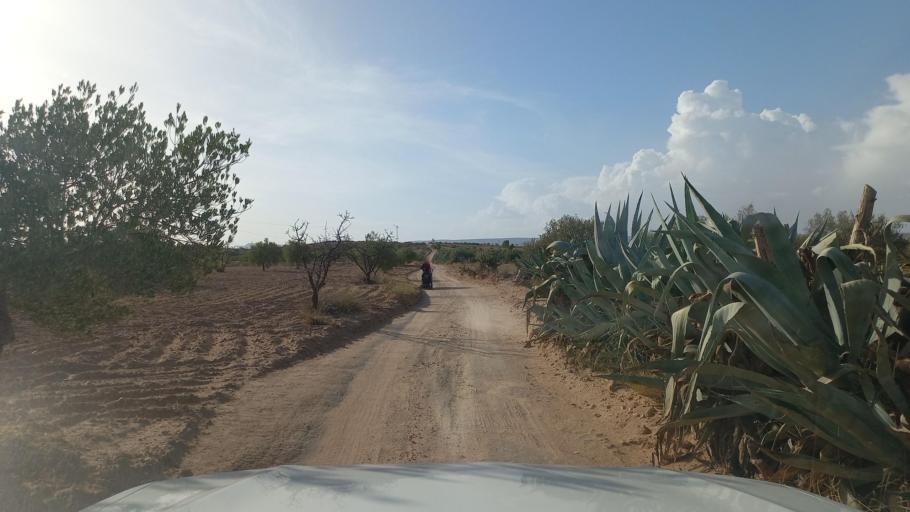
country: TN
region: Al Qasrayn
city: Kasserine
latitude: 35.2322
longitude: 8.9224
